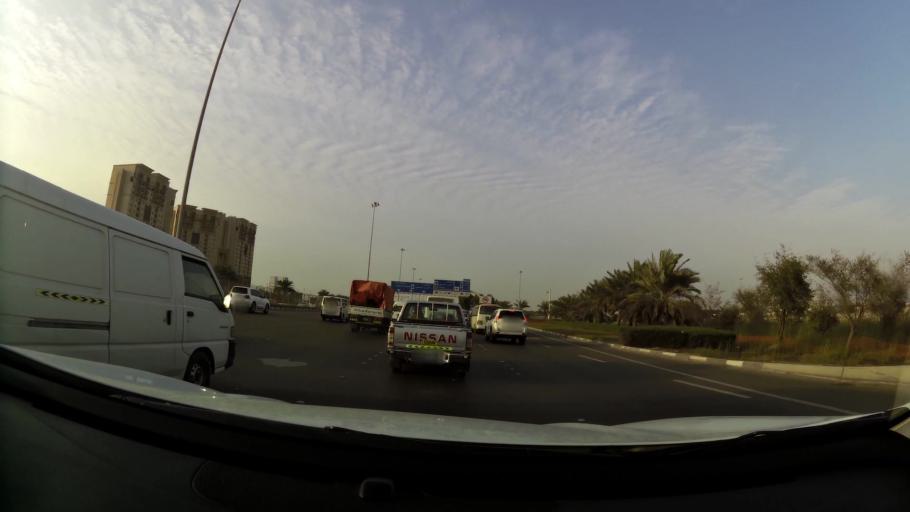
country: AE
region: Abu Dhabi
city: Abu Dhabi
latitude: 24.3819
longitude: 54.5247
